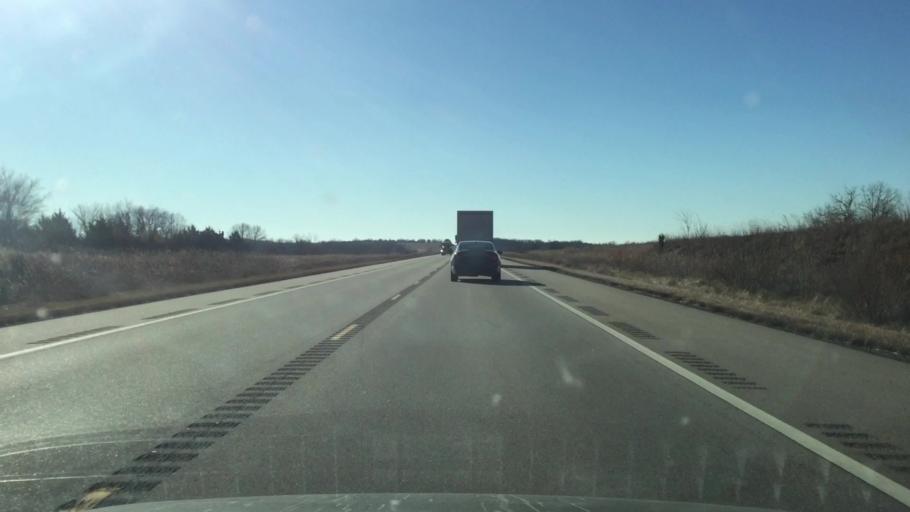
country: US
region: Kansas
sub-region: Allen County
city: Iola
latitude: 38.0309
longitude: -95.3808
